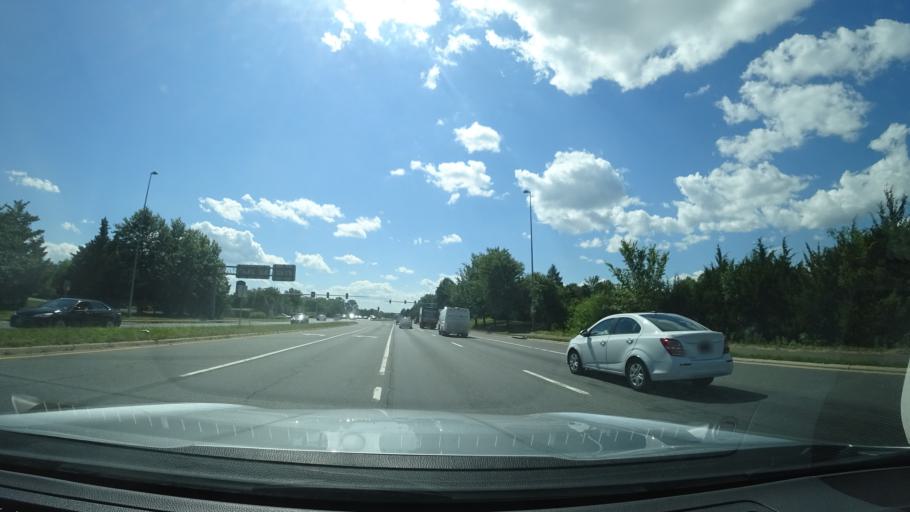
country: US
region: Virginia
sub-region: Loudoun County
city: Sterling
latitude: 38.9792
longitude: -77.4331
